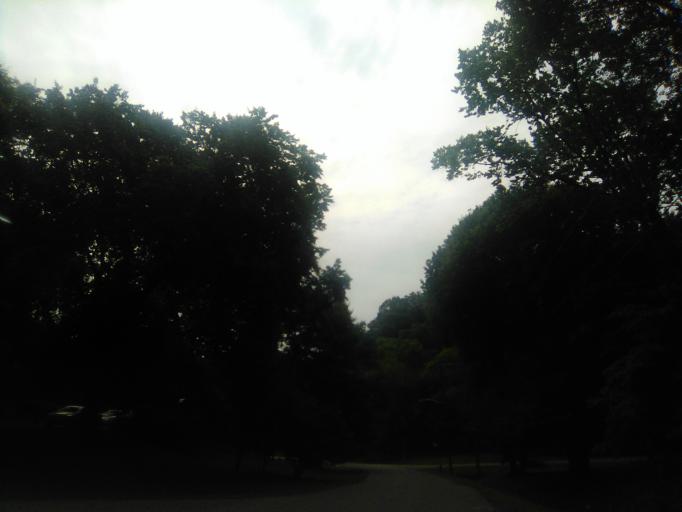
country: US
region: Tennessee
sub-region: Davidson County
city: Belle Meade
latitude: 36.0916
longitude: -86.9023
